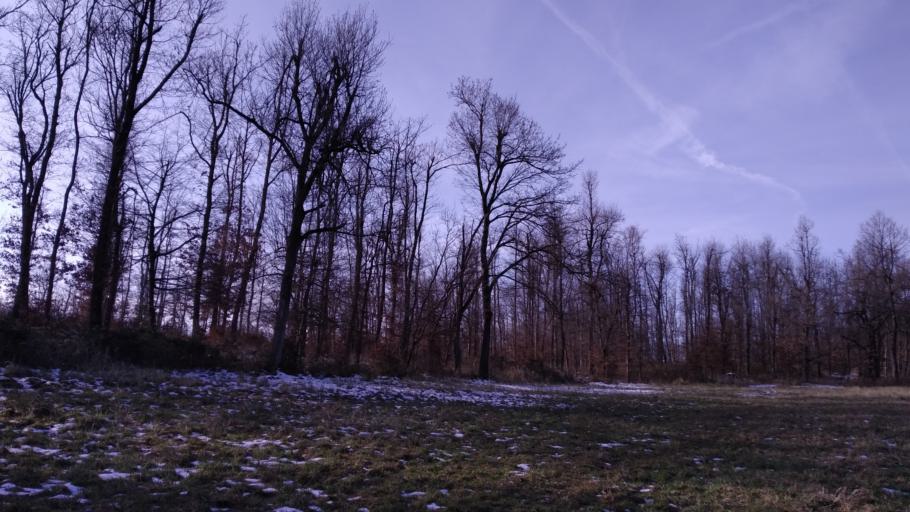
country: HU
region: Pest
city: Pilisszentkereszt
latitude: 47.7112
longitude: 18.8865
